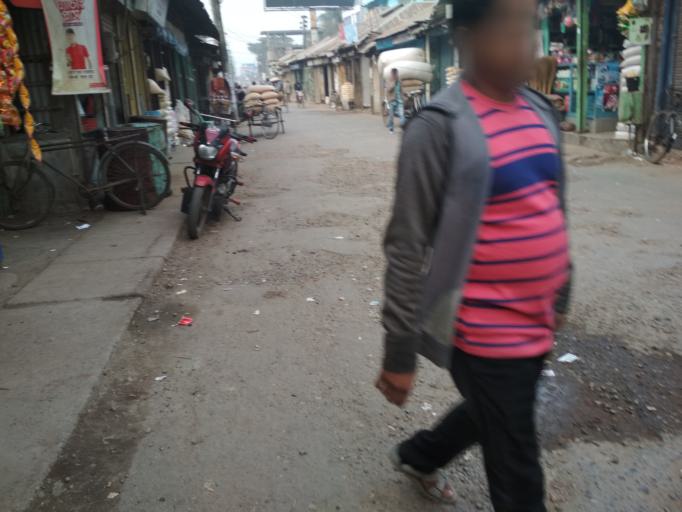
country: BD
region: Chittagong
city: Lakshmipur
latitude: 22.9398
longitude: 90.8281
